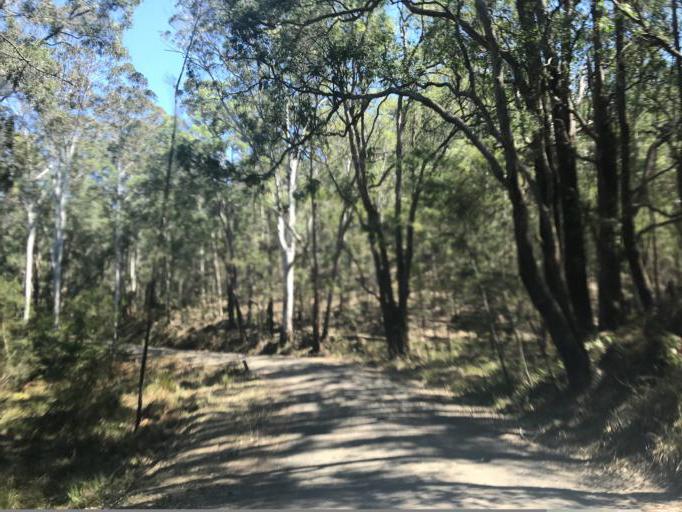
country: AU
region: New South Wales
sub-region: Wyong Shire
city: Little Jilliby
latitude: -33.1976
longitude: 151.0047
